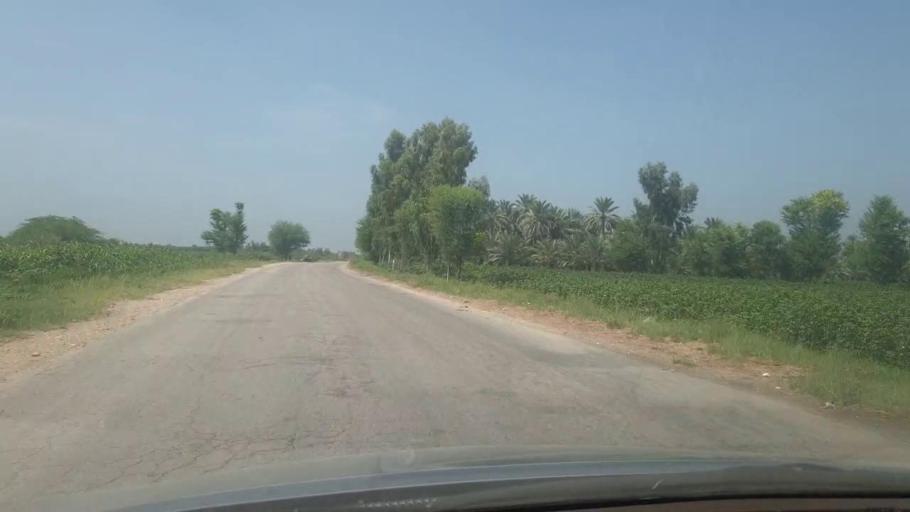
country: PK
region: Sindh
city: Ranipur
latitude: 27.2558
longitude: 68.5868
